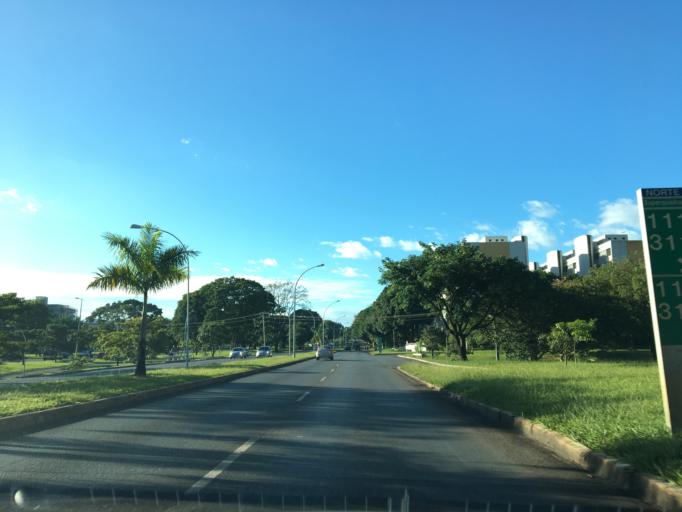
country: BR
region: Federal District
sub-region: Brasilia
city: Brasilia
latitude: -15.7515
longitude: -47.8883
